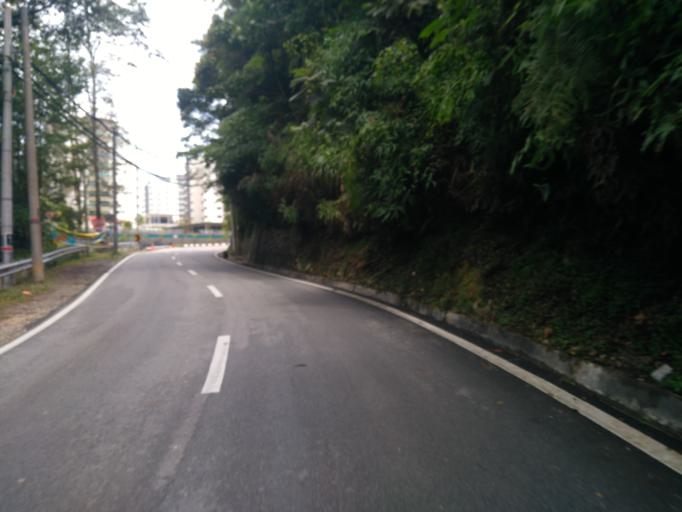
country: MY
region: Pahang
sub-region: Cameron Highlands
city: Tanah Rata
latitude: 4.4733
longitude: 101.3786
